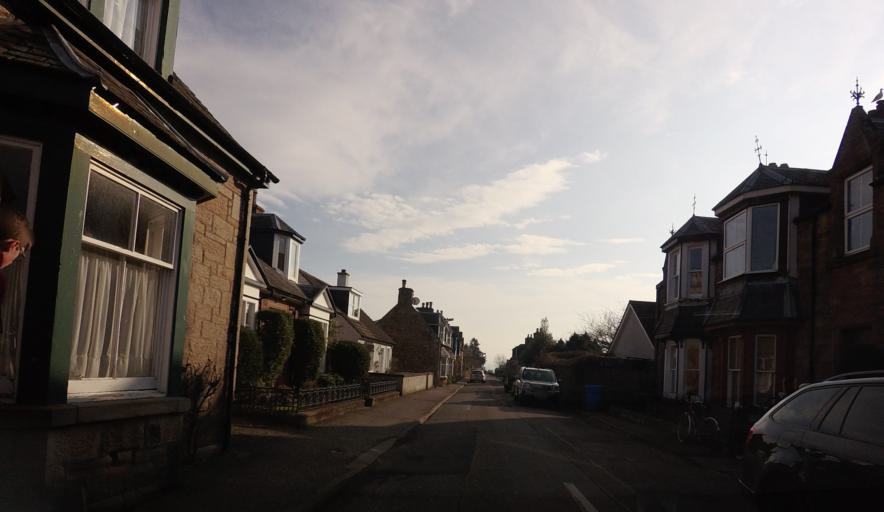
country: GB
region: Scotland
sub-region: Highland
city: Fortrose
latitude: 57.5819
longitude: -4.1296
